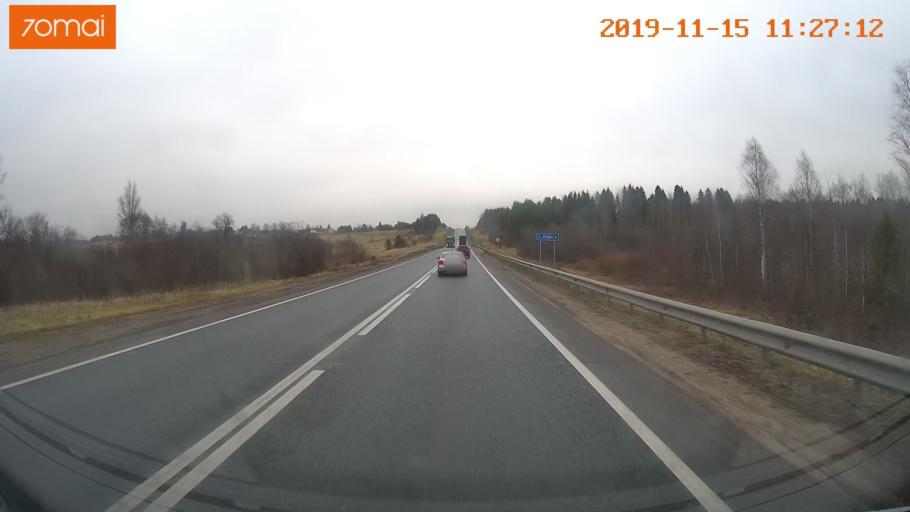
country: RU
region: Vologda
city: Molochnoye
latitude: 59.1691
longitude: 39.4619
